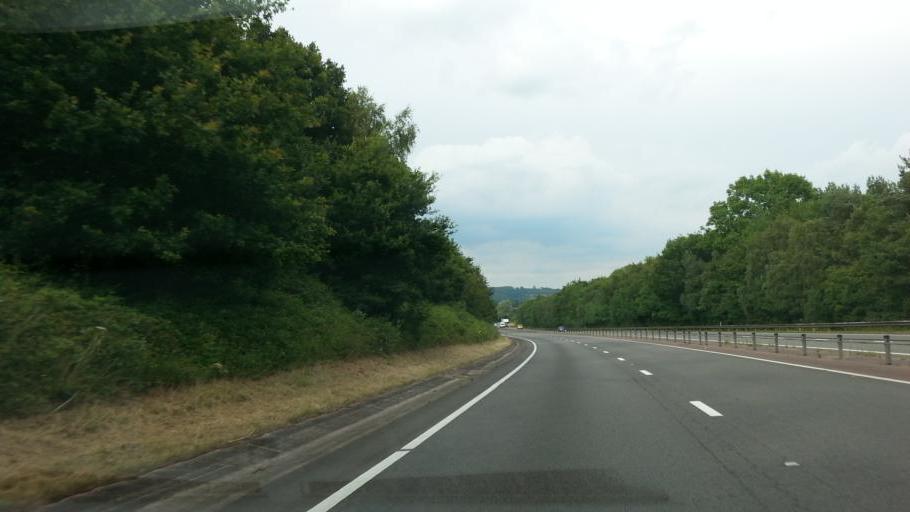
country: GB
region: Wales
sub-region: Monmouthshire
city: Mitchel Troy
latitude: 51.7787
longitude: -2.7929
